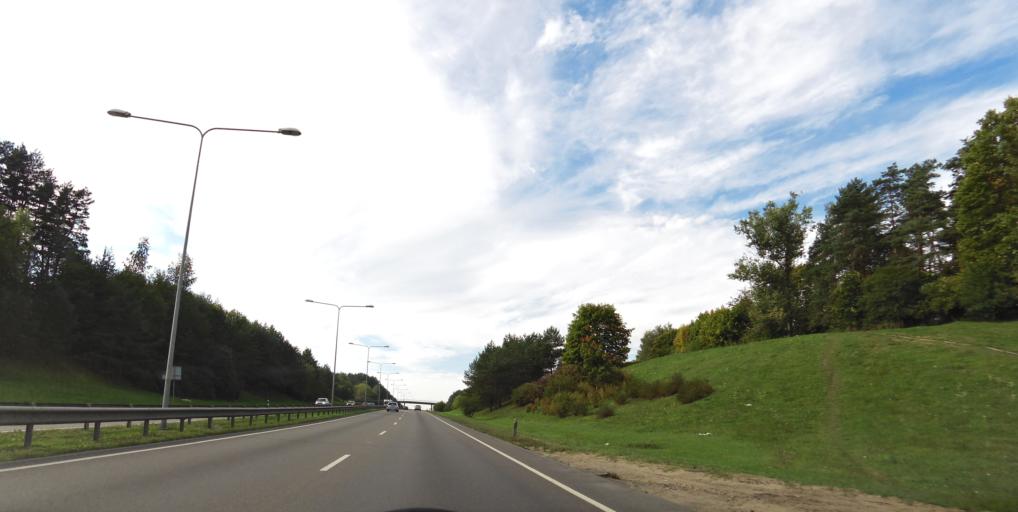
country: LT
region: Vilnius County
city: Lazdynai
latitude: 54.6718
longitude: 25.2195
